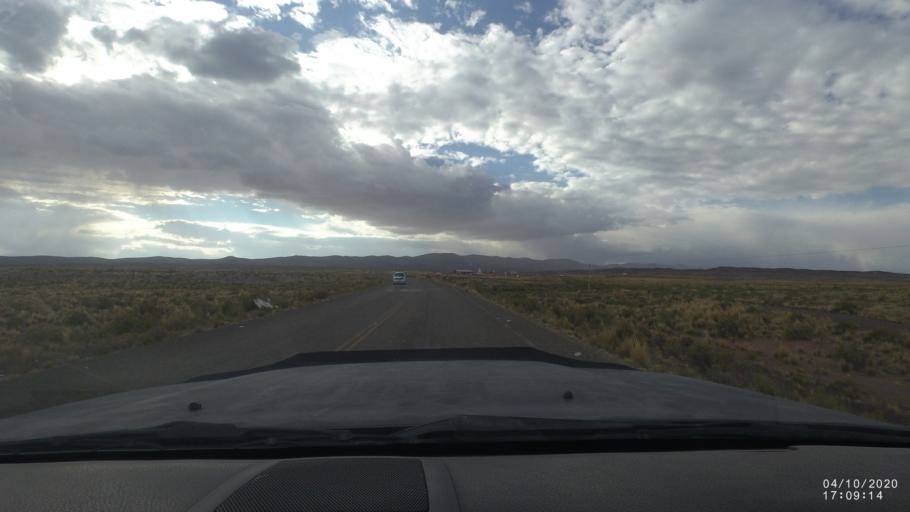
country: BO
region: Oruro
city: Oruro
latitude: -18.3404
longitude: -67.5807
